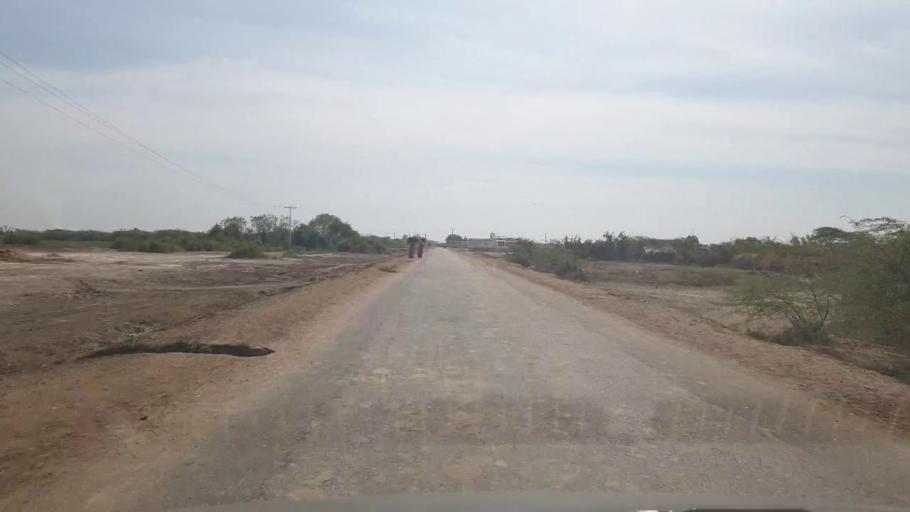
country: PK
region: Sindh
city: Umarkot
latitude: 25.3334
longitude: 69.5919
